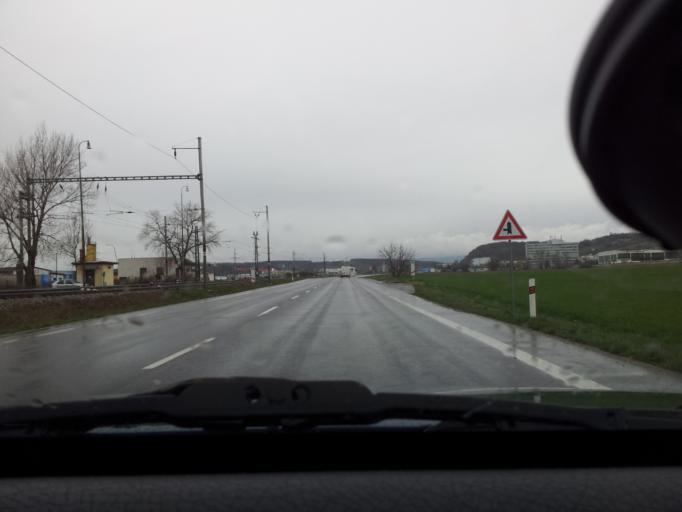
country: SK
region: Nitriansky
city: Tlmace
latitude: 48.2834
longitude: 18.5465
